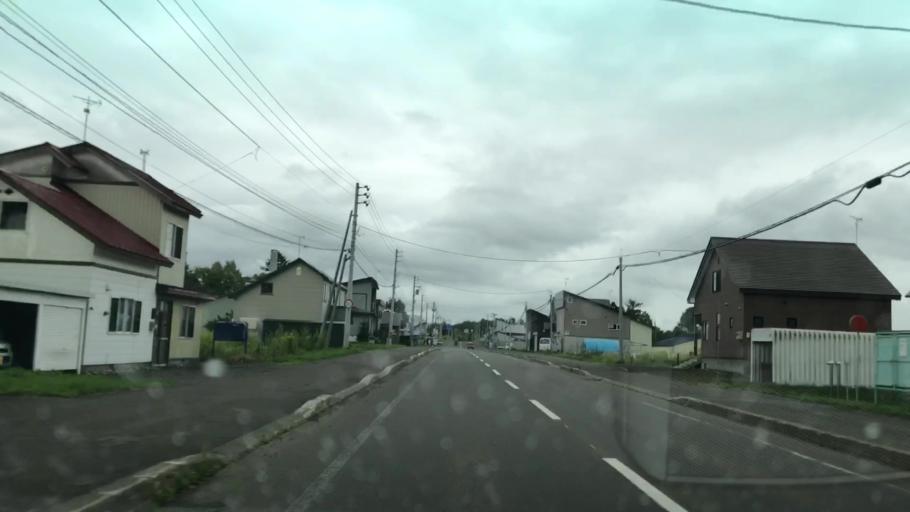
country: JP
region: Hokkaido
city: Niseko Town
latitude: 42.7974
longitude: 140.7078
